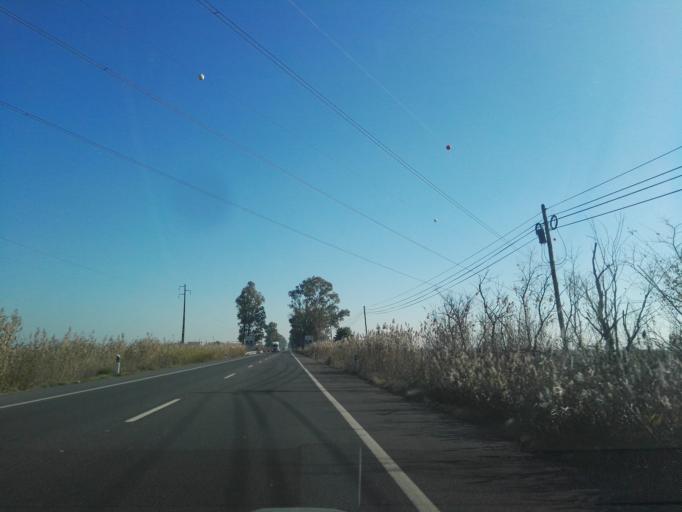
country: PT
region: Lisbon
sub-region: Vila Franca de Xira
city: Vila Franca de Xira
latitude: 38.9447
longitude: -8.9532
